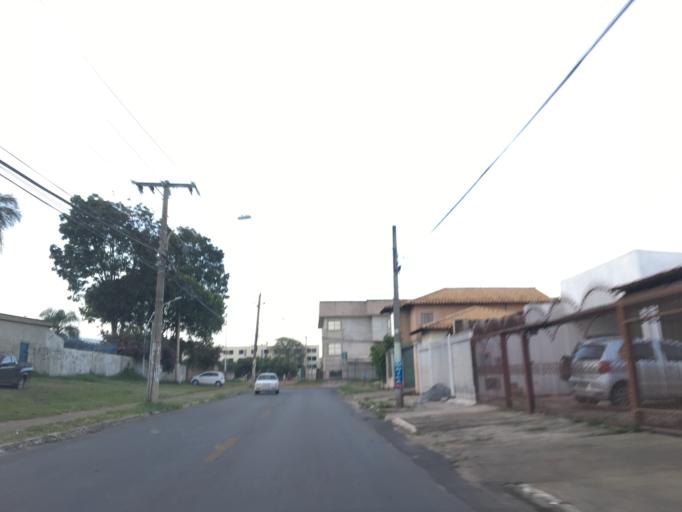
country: BR
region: Federal District
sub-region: Brasilia
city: Brasilia
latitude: -15.8156
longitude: -47.9778
